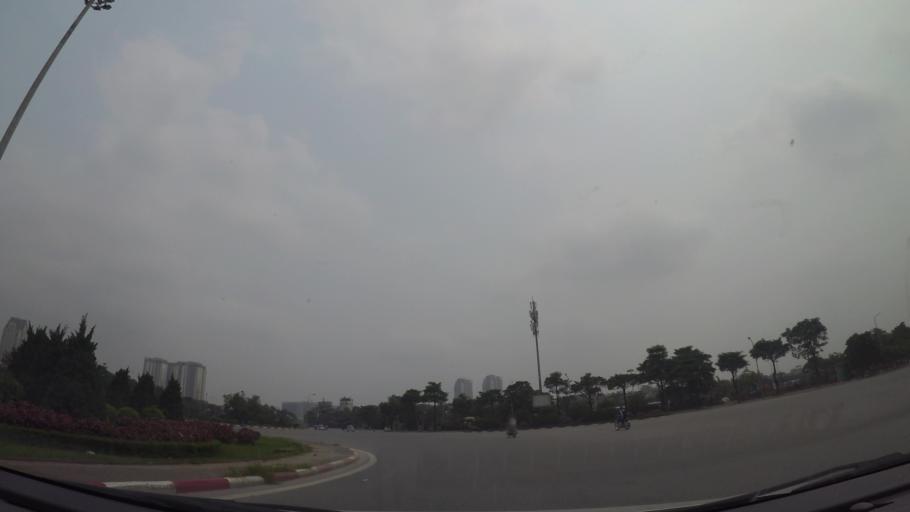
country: VN
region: Ha Noi
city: Cau Dien
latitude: 21.0173
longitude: 105.7668
